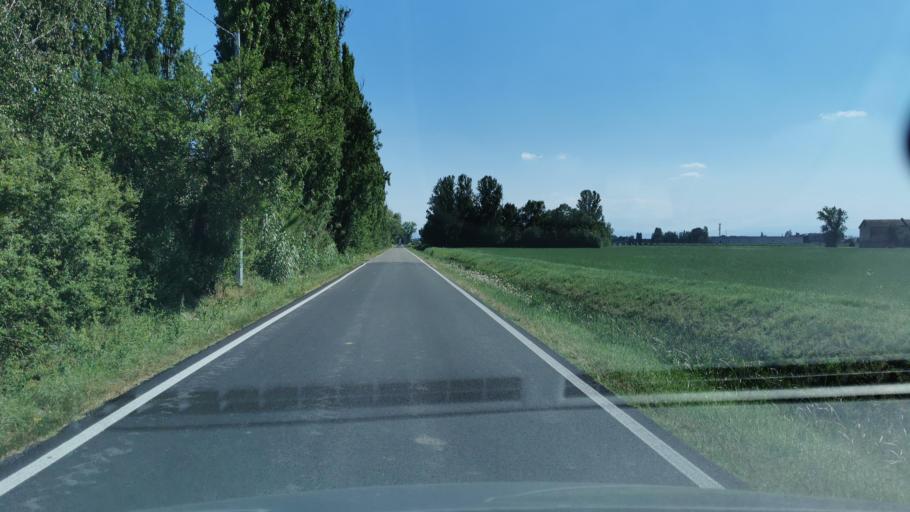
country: IT
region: Emilia-Romagna
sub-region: Provincia di Modena
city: Limidi
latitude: 44.7760
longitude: 10.9179
